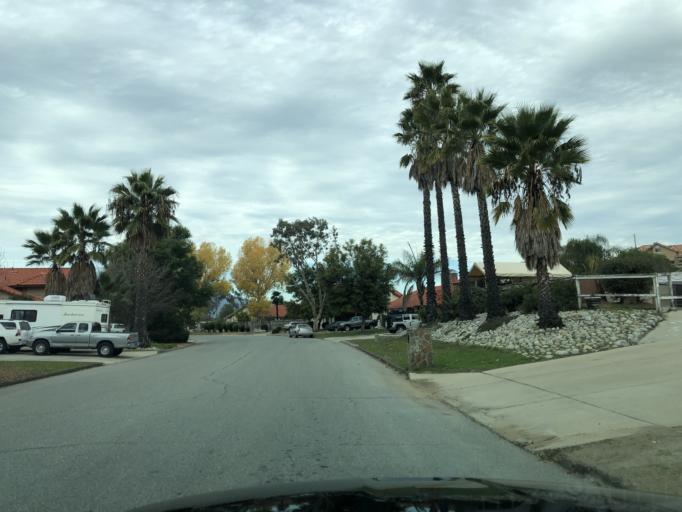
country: US
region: California
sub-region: Riverside County
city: Wildomar
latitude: 33.6175
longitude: -117.2850
